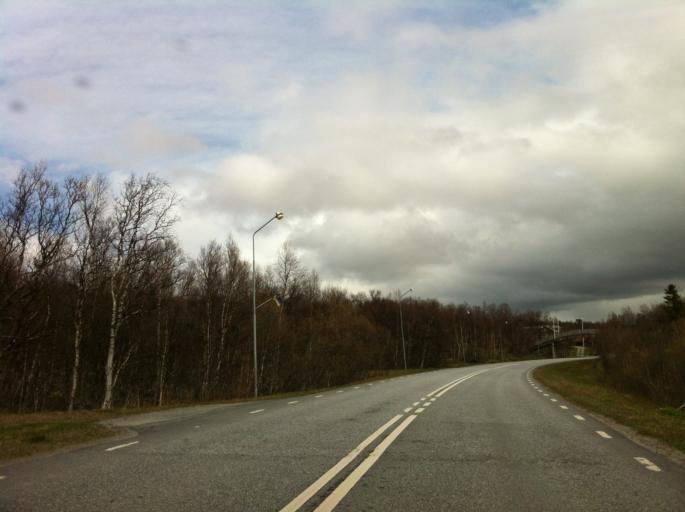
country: NO
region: Sor-Trondelag
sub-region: Tydal
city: Aas
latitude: 62.5499
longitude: 12.3058
